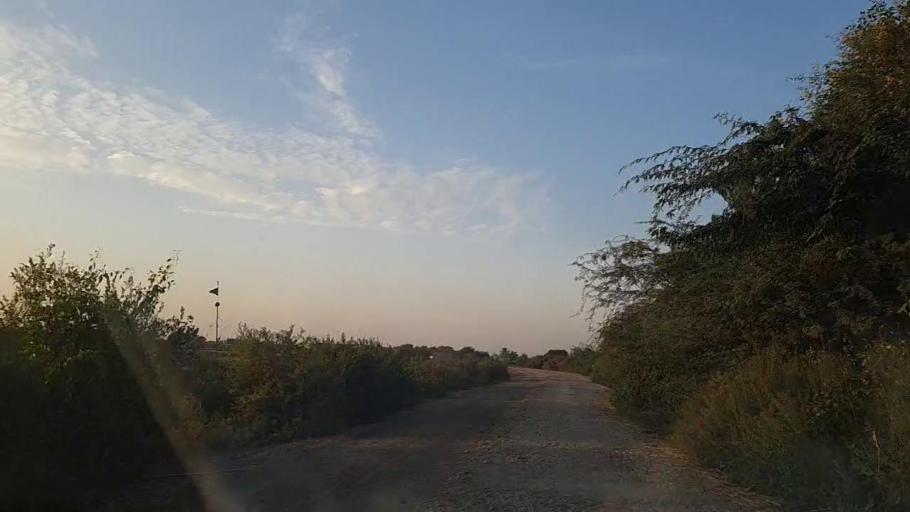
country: PK
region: Sindh
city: Chuhar Jamali
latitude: 24.4549
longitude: 68.1171
